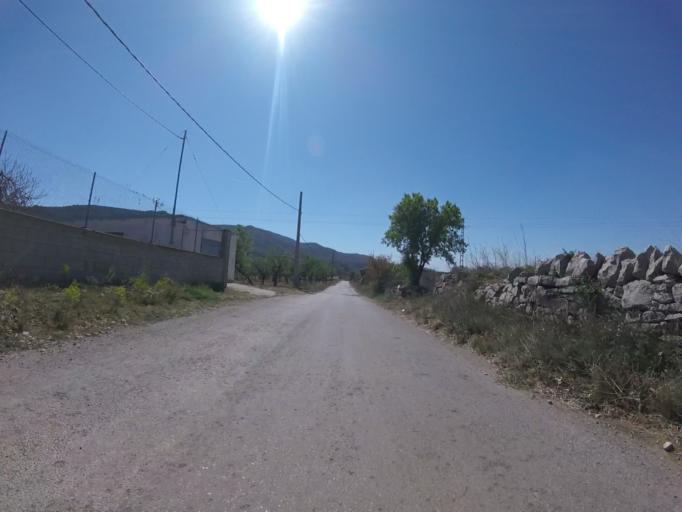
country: ES
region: Valencia
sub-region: Provincia de Castello
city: Chert/Xert
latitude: 40.4152
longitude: 0.1750
